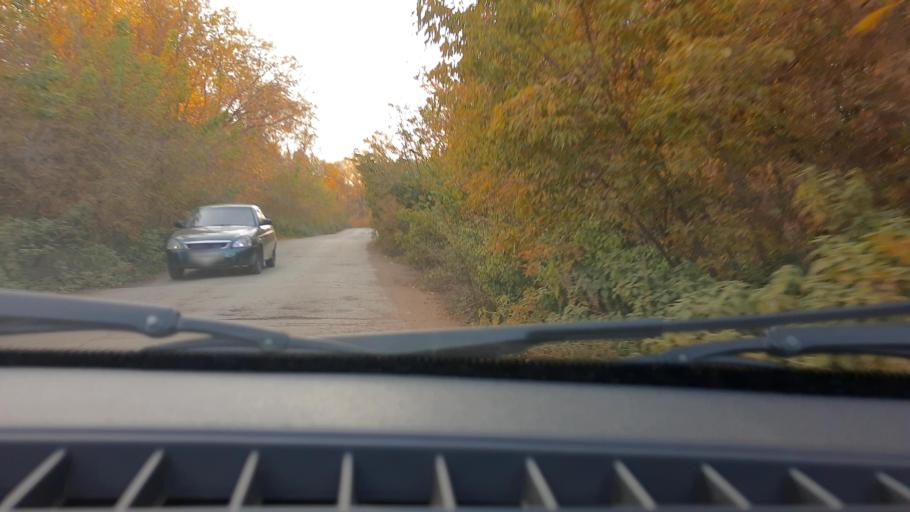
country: RU
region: Bashkortostan
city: Ufa
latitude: 54.7981
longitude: 56.1781
